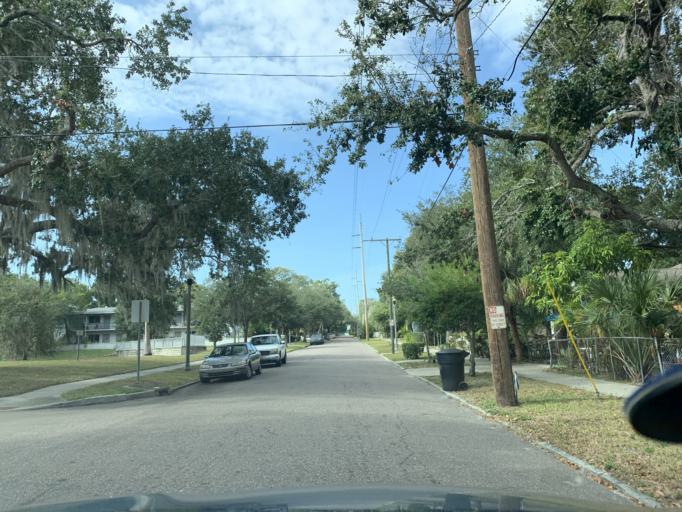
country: US
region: Florida
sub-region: Pinellas County
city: Saint Petersburg
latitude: 27.7595
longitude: -82.6403
